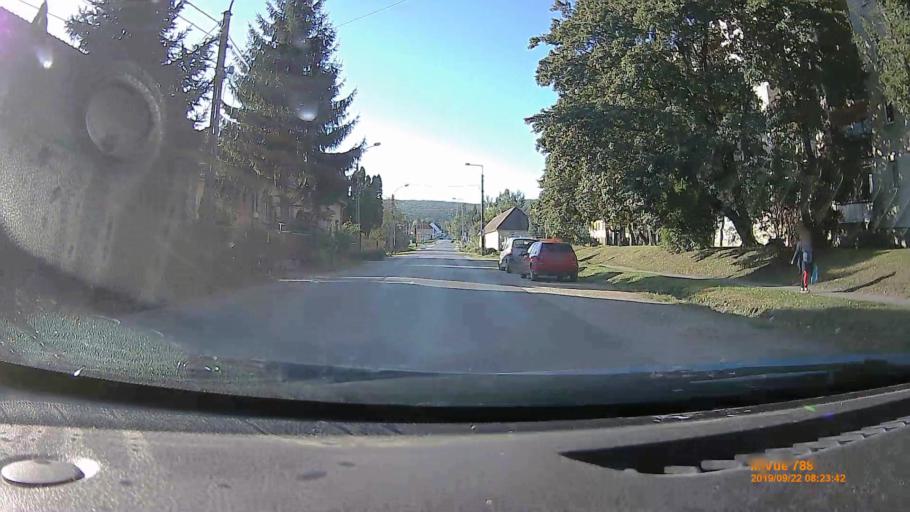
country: HU
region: Borsod-Abauj-Zemplen
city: Miskolc
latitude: 48.0957
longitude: 20.7110
